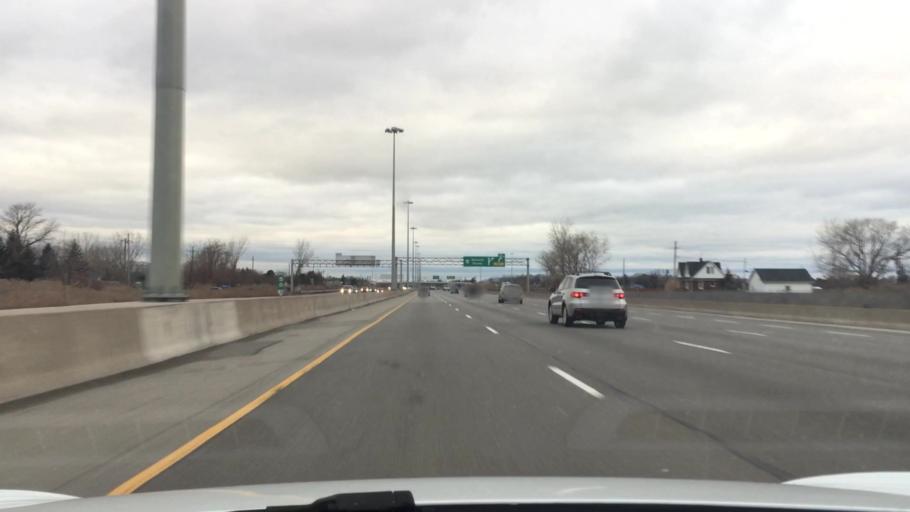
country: CA
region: Ontario
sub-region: Regional Municipality of Niagara
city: St. Catharines
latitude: 43.1784
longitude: -79.2968
